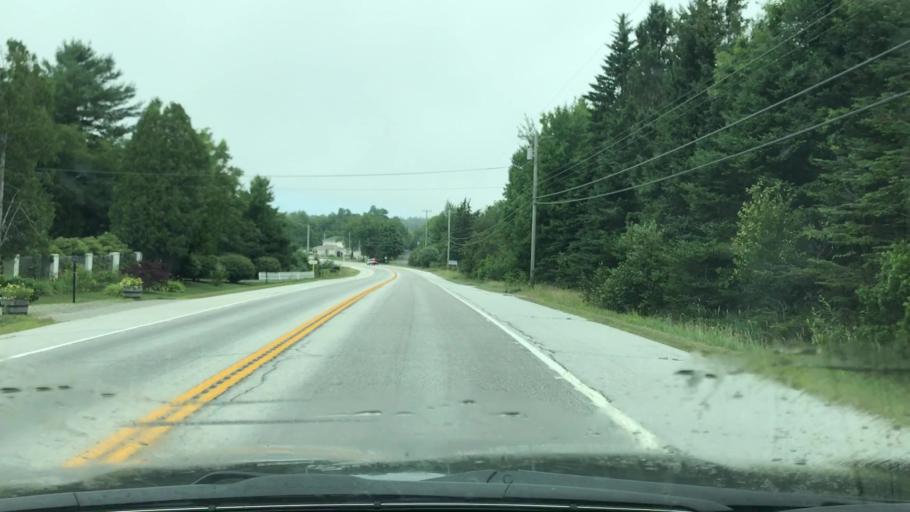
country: US
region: Maine
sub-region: Waldo County
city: Northport
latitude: 44.3309
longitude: -68.9575
